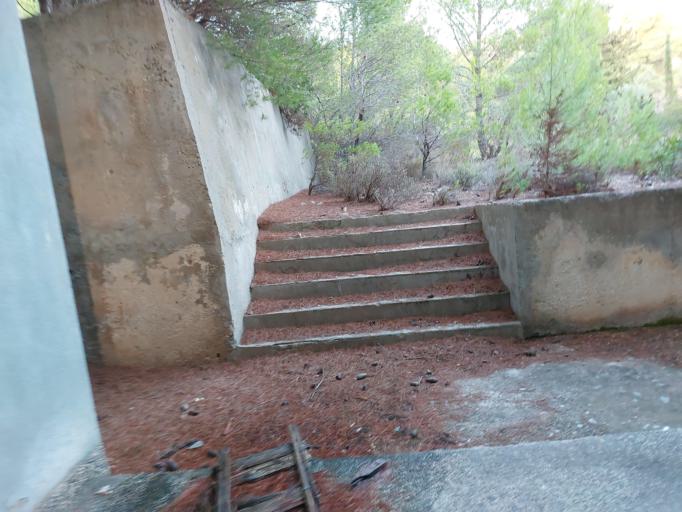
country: HR
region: Dubrovacko-Neretvanska
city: Smokvica
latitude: 42.7392
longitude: 16.8281
